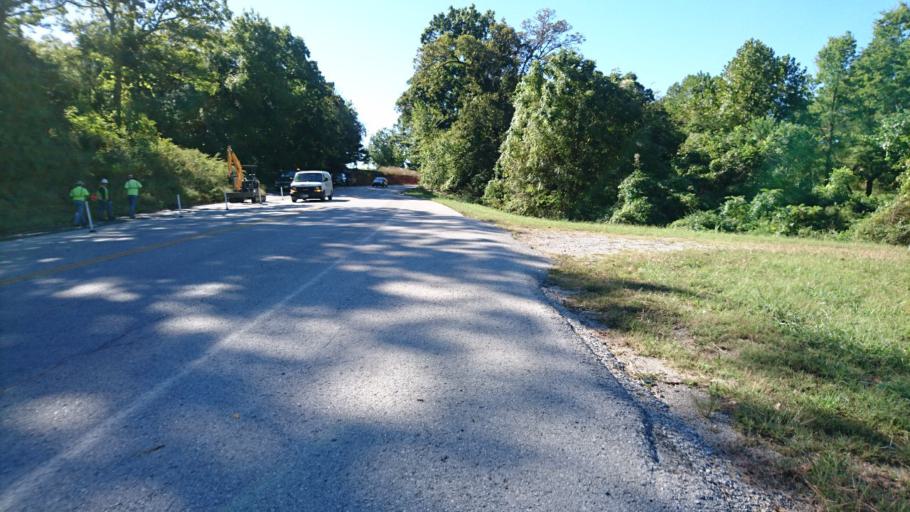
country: US
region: Missouri
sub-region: Jasper County
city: Joplin
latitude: 37.0989
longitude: -94.4948
